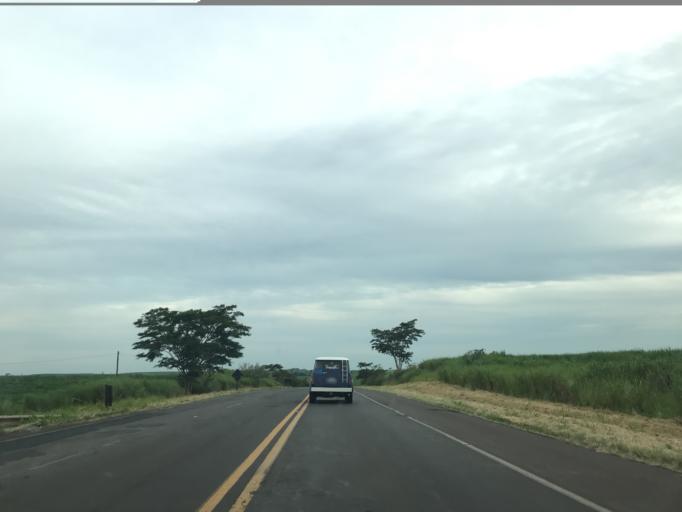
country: BR
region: Sao Paulo
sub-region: Tupa
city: Tupa
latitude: -21.6248
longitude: -50.4857
